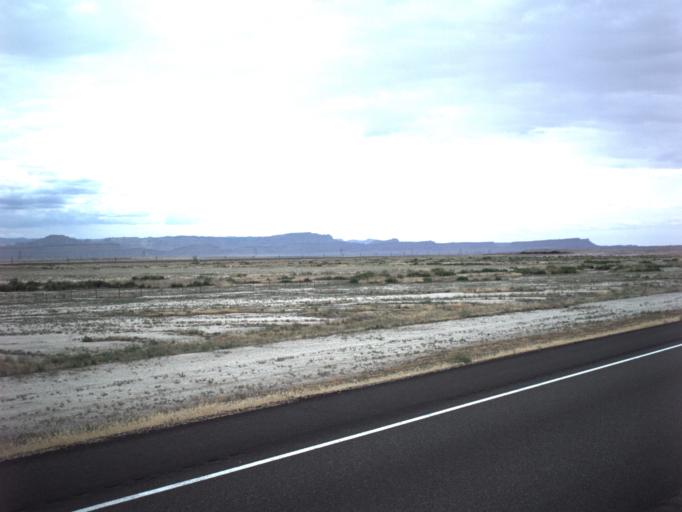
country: US
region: Utah
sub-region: Carbon County
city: East Carbon City
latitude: 38.9972
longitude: -110.2614
